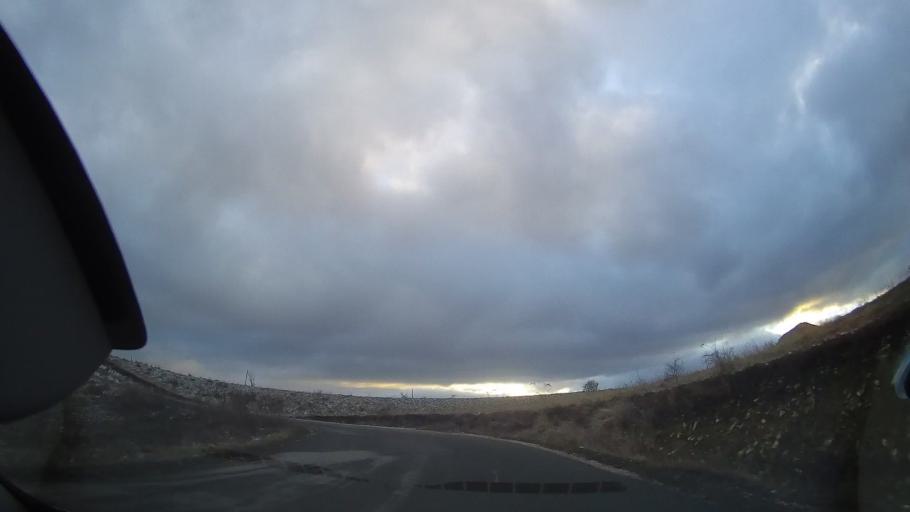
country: RO
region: Cluj
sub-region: Comuna Manastireni
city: Manastireni
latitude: 46.7795
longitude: 23.0548
